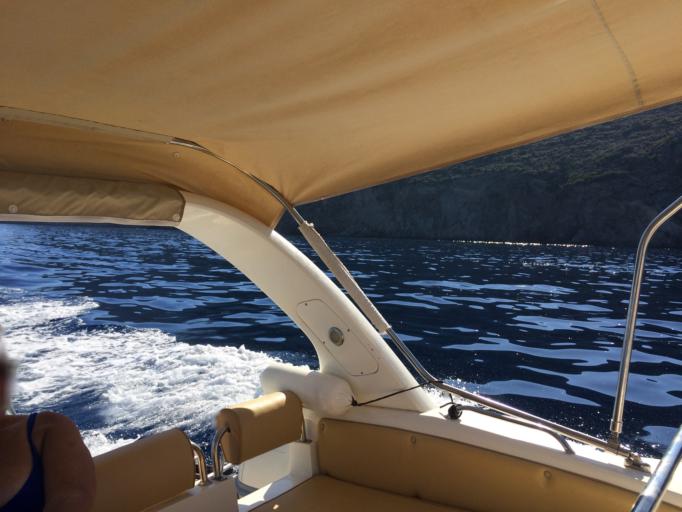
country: IT
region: Tuscany
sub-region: Provincia di Livorno
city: Capraia Isola
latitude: 43.0380
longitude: 9.8481
